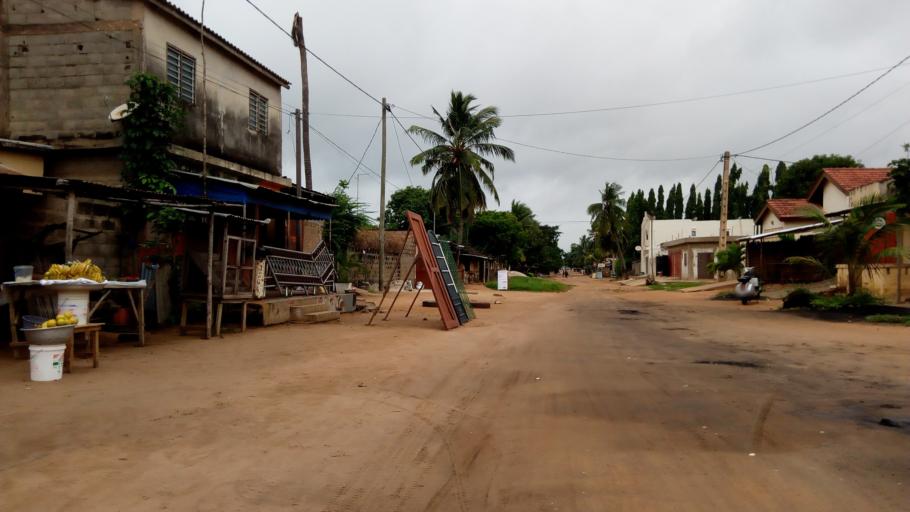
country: TG
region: Maritime
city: Lome
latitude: 6.1787
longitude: 1.1788
